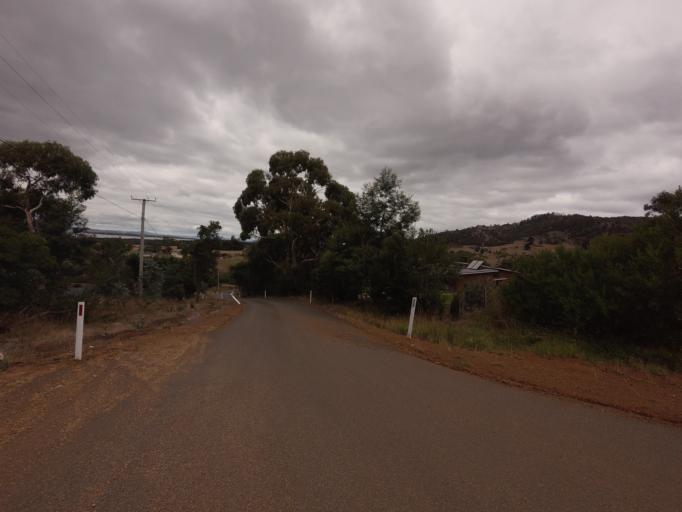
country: AU
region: Tasmania
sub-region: Clarence
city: Cambridge
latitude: -42.7884
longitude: 147.4142
